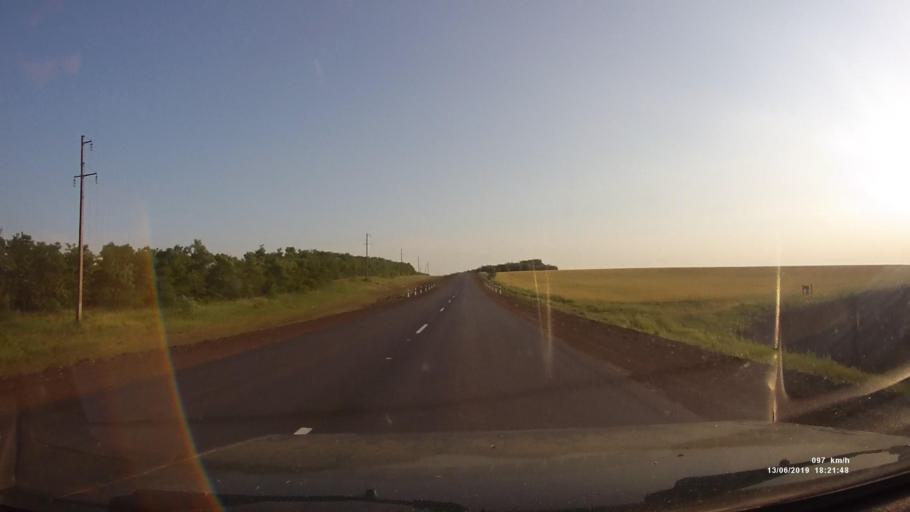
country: RU
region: Rostov
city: Kazanskaya
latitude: 49.8664
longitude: 41.2859
